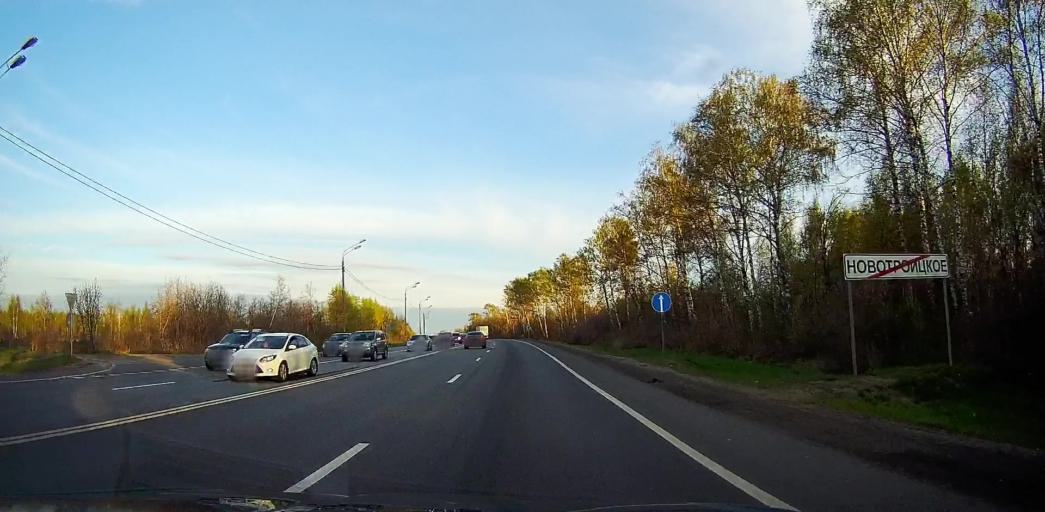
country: RU
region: Moskovskaya
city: Troitskoye
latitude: 55.2706
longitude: 38.4994
